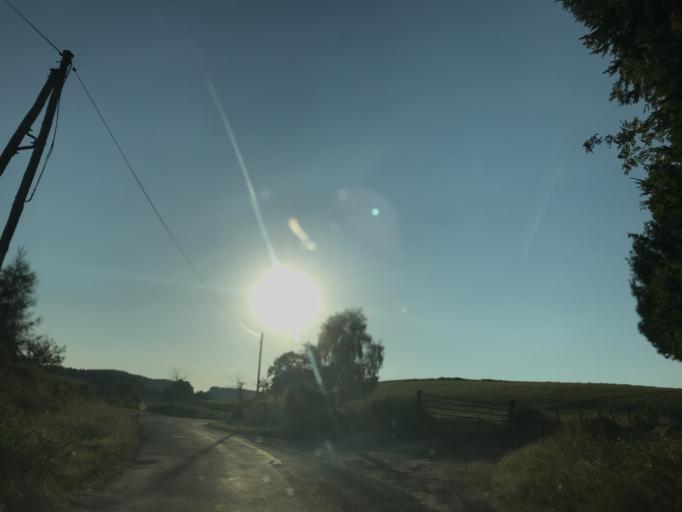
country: FR
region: Auvergne
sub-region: Departement du Puy-de-Dome
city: Celles-sur-Durolle
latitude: 45.8397
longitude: 3.6330
